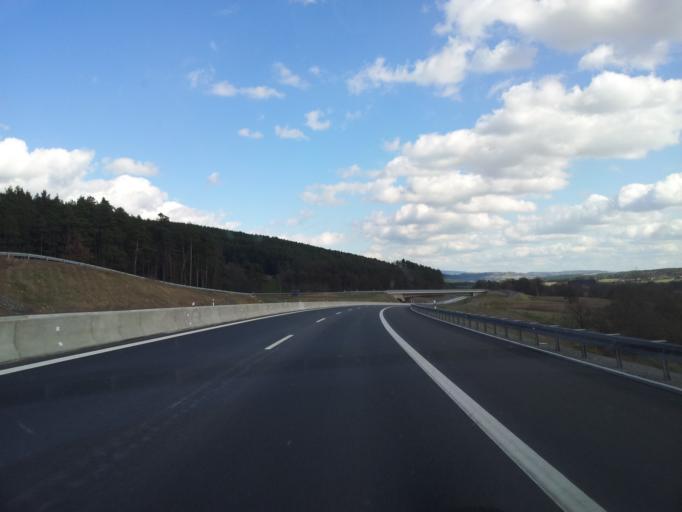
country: DE
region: Bavaria
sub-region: Upper Franconia
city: Neudrossenfeld
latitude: 50.0392
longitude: 11.5093
